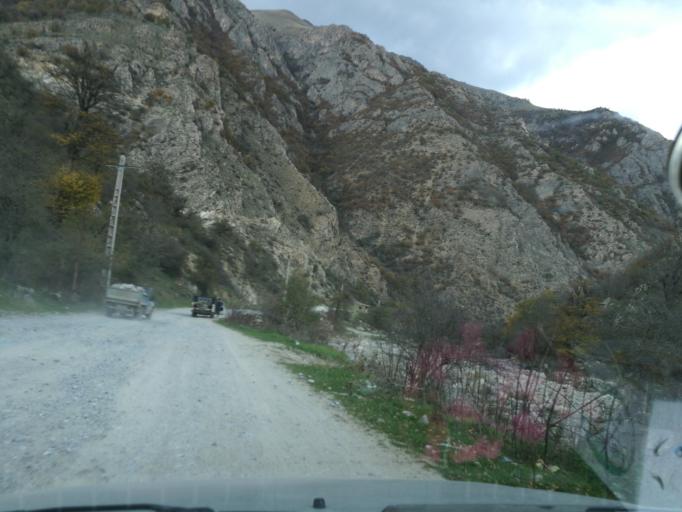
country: IR
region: Mazandaran
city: `Abbasabad
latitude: 36.4446
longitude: 51.0633
